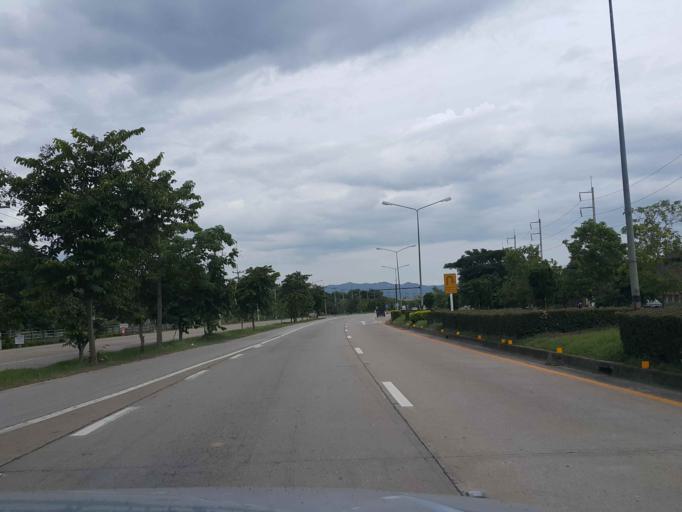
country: TH
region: Lampang
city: Lampang
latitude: 18.2880
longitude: 99.4439
